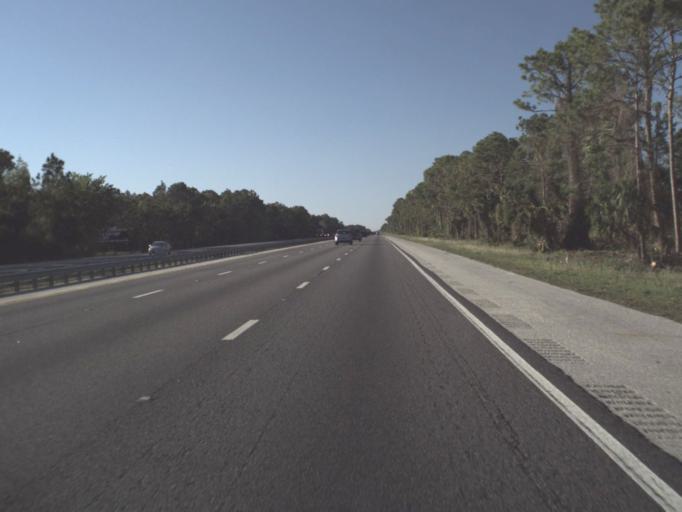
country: US
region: Florida
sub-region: Flagler County
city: Flagler Beach
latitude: 29.4410
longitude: -81.1703
